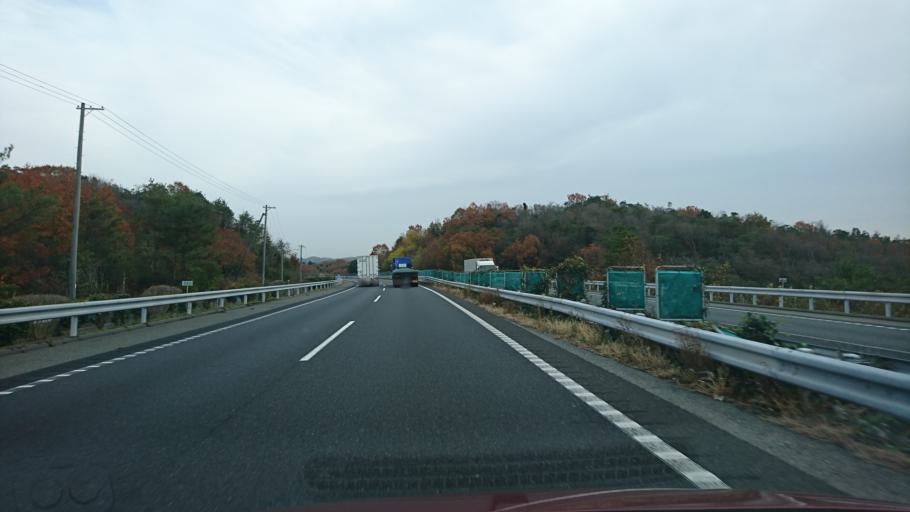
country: JP
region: Hyogo
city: Miki
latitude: 34.8171
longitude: 134.9872
